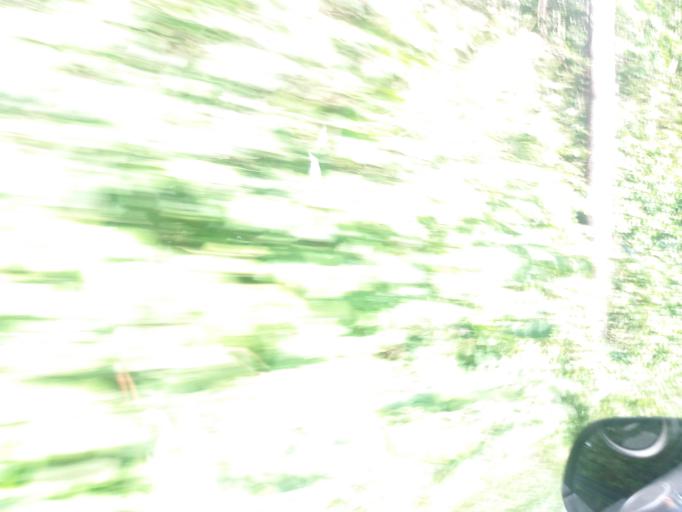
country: IE
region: Leinster
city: Hartstown
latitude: 53.3699
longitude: -6.4099
